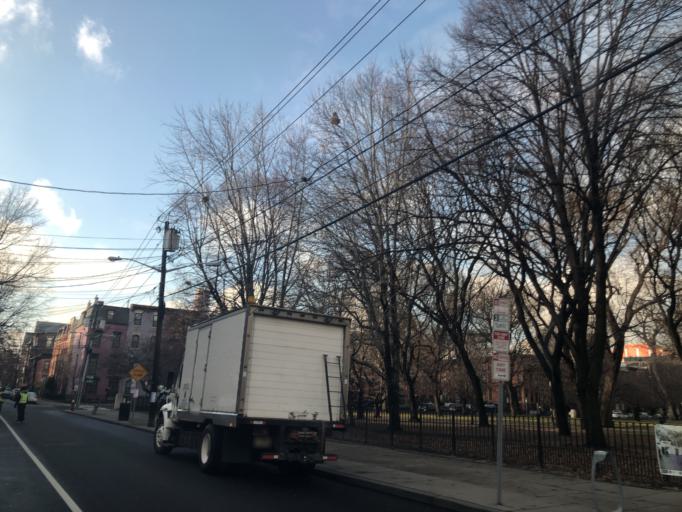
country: US
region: New Jersey
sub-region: Hudson County
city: Hoboken
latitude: 40.7269
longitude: -74.0453
